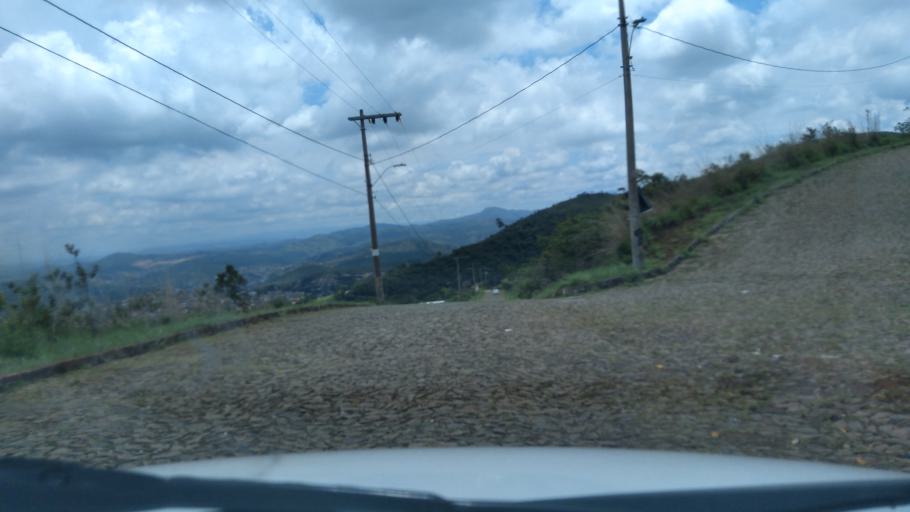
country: BR
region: Minas Gerais
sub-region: Belo Horizonte
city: Belo Horizonte
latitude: -19.9313
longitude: -43.8850
